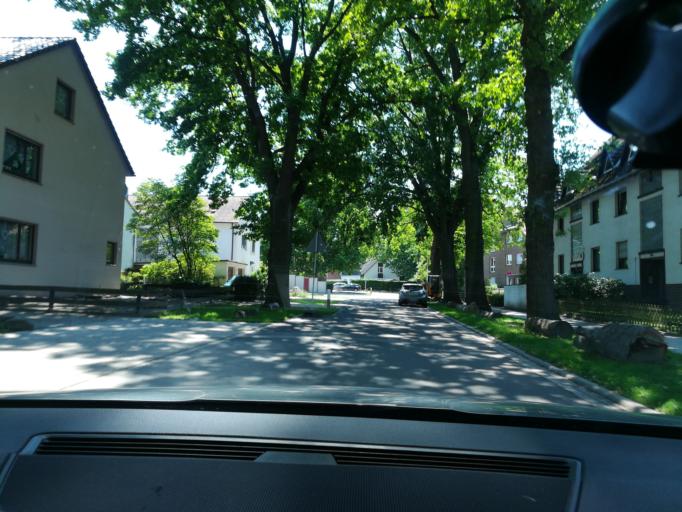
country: DE
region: North Rhine-Westphalia
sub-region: Regierungsbezirk Detmold
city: Minden
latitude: 52.3042
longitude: 8.9078
